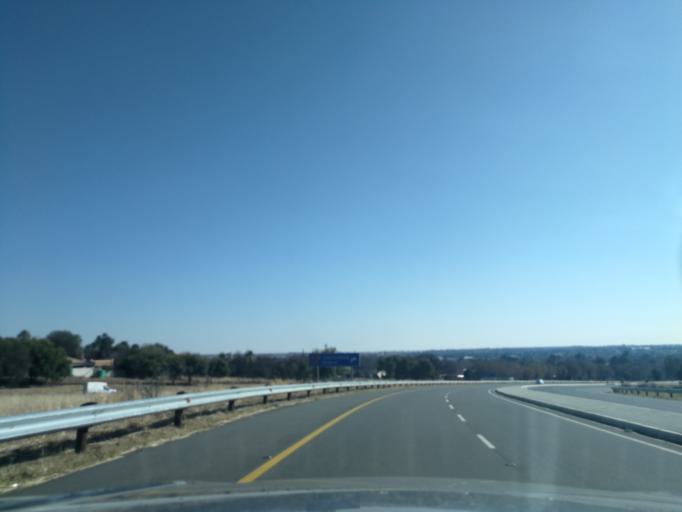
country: ZA
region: Orange Free State
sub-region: Fezile Dabi District Municipality
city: Kroonstad
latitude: -27.6865
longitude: 27.2411
